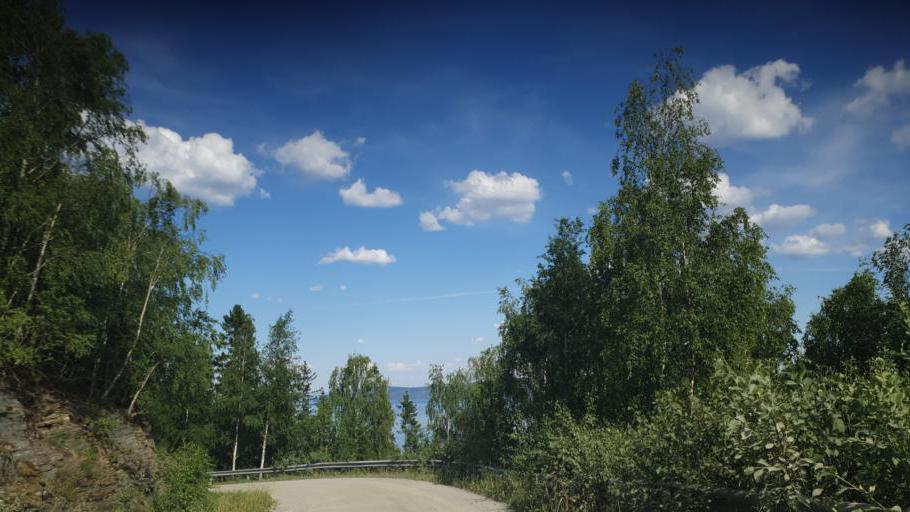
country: NO
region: Nord-Trondelag
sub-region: Leksvik
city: Leksvik
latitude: 63.6777
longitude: 10.6585
